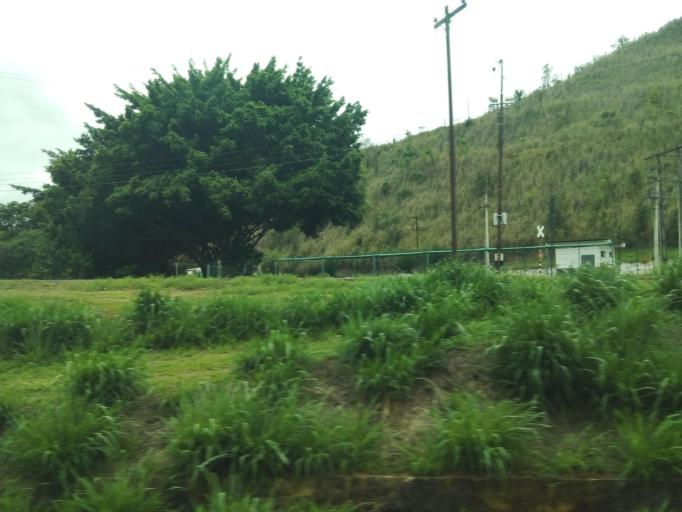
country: BR
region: Minas Gerais
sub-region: Nova Era
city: Nova Era
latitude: -19.7270
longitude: -43.0079
